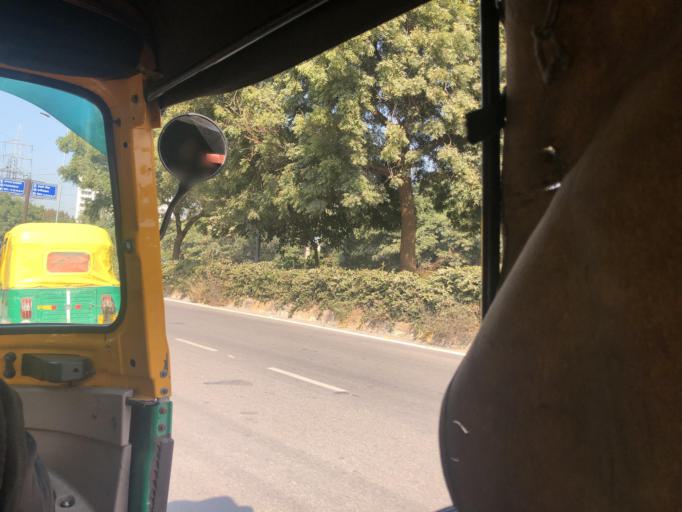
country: IN
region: Haryana
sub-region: Gurgaon
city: Gurgaon
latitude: 28.4462
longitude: 77.0808
